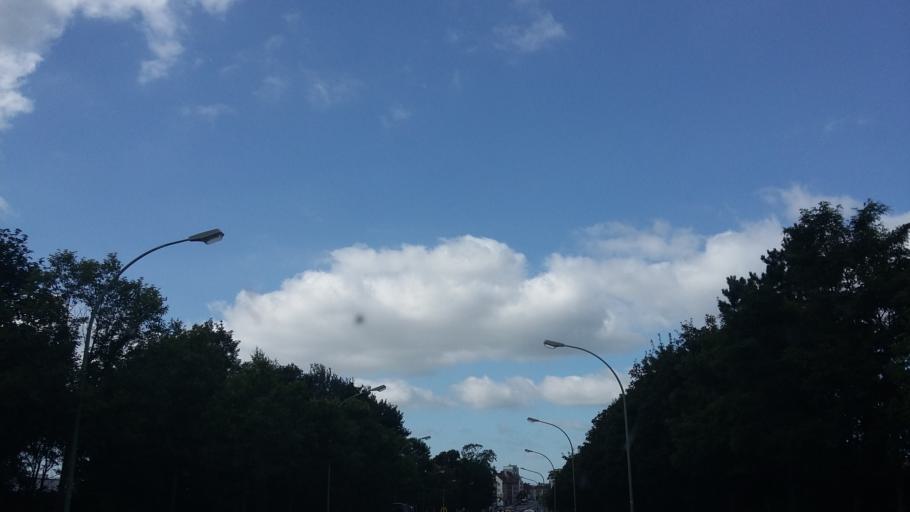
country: DE
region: Bremen
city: Bremerhaven
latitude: 53.5236
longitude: 8.5904
